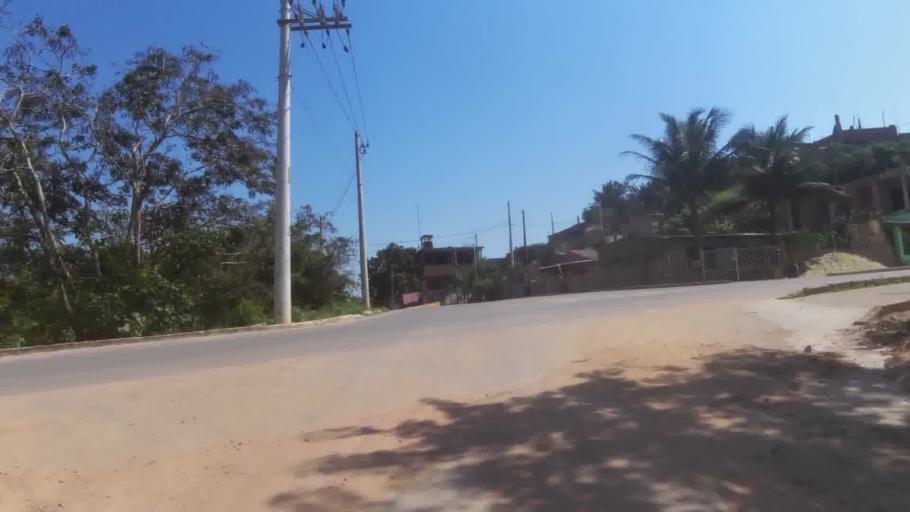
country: BR
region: Espirito Santo
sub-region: Itapemirim
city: Itapemirim
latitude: -21.0175
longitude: -40.8278
